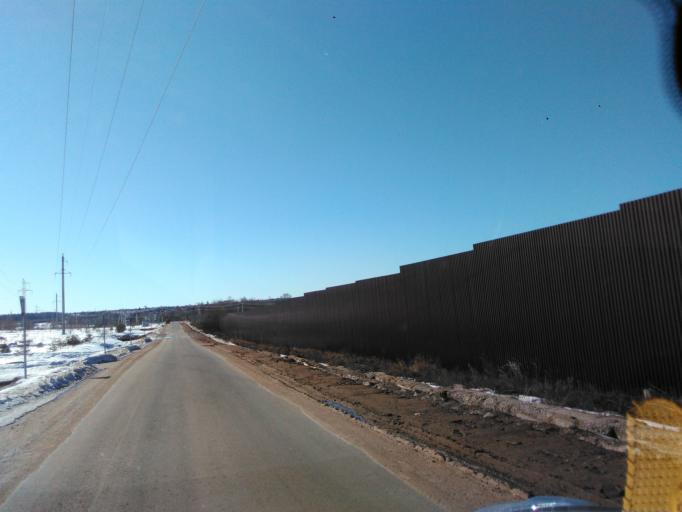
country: RU
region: Moskovskaya
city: Yermolino
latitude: 56.1525
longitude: 37.4820
